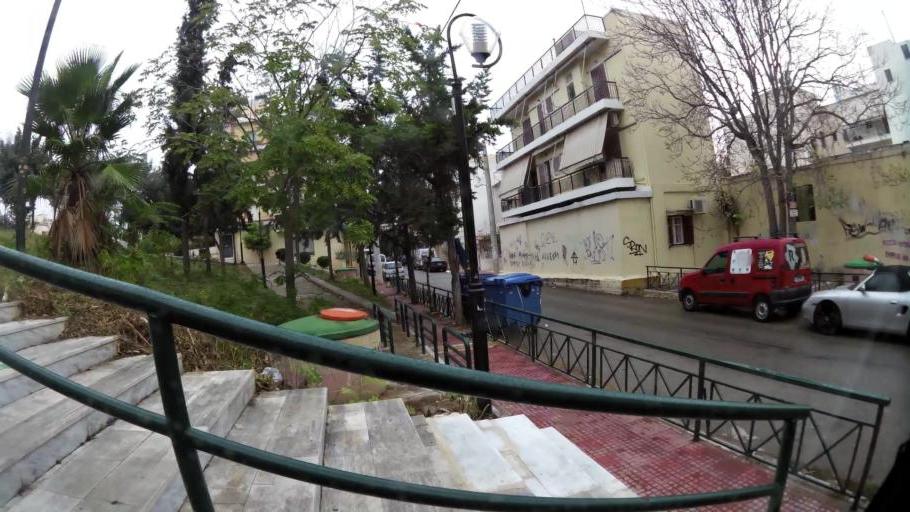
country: GR
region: Attica
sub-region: Nomarchia Athinas
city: Agioi Anargyroi
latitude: 38.0387
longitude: 23.7278
